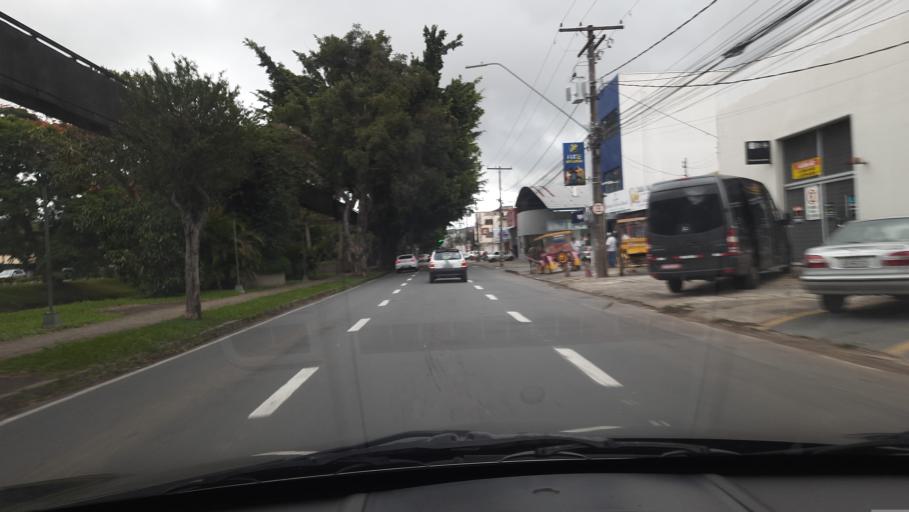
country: BR
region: Minas Gerais
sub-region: Pocos De Caldas
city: Pocos de Caldas
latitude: -21.7852
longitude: -46.5840
